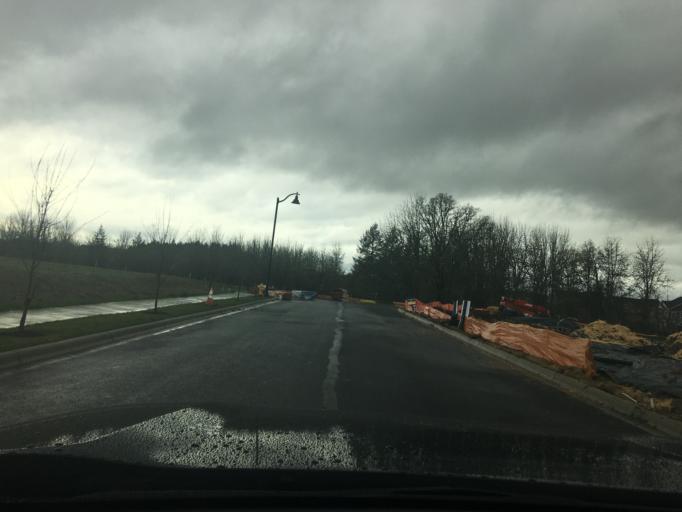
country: US
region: Oregon
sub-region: Washington County
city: Bethany
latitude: 45.5714
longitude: -122.8452
